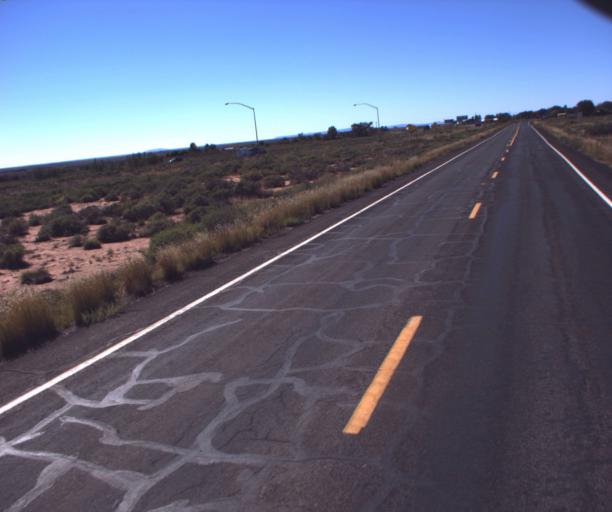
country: US
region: Arizona
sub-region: Navajo County
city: Joseph City
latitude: 34.9557
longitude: -110.3156
